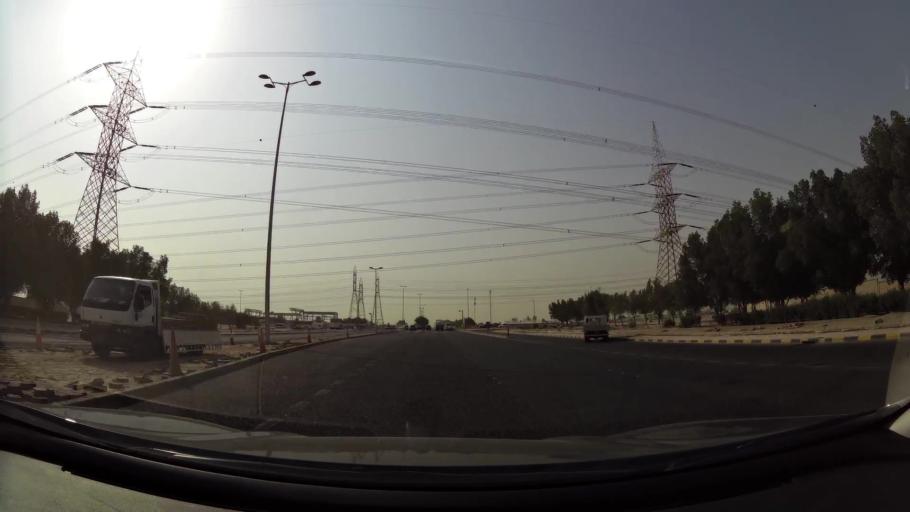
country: KW
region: Al Asimah
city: Ar Rabiyah
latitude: 29.2971
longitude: 47.8321
